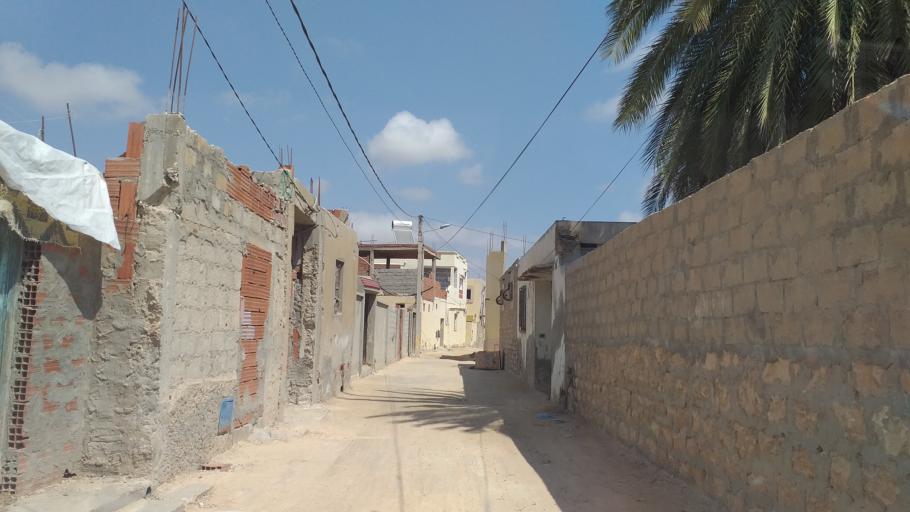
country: TN
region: Qabis
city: Gabes
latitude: 33.9433
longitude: 10.0648
